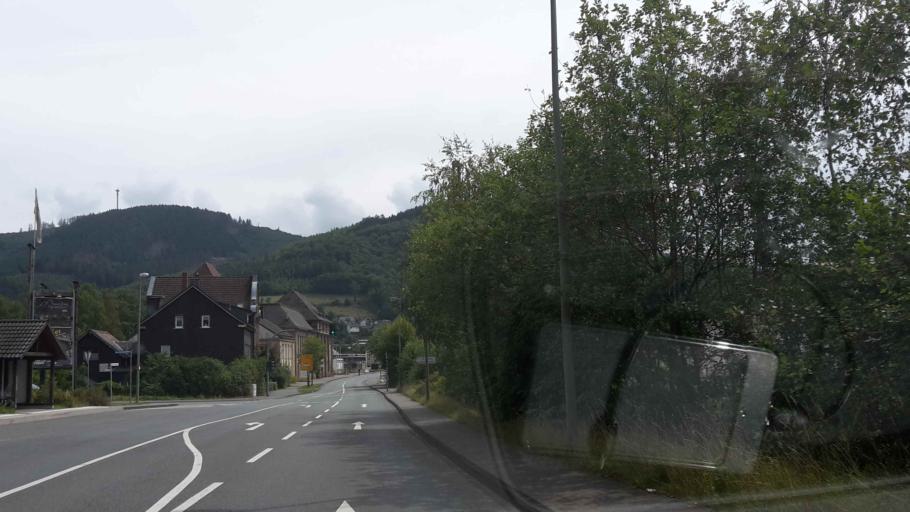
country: DE
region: North Rhine-Westphalia
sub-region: Regierungsbezirk Arnsberg
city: Lennestadt
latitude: 51.1259
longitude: 8.0603
